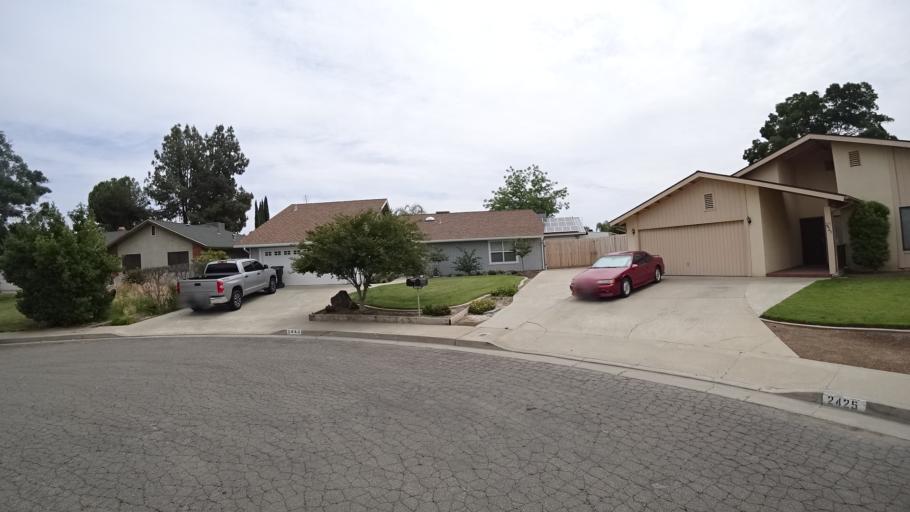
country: US
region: California
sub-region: Kings County
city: Hanford
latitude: 36.3562
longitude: -119.6432
